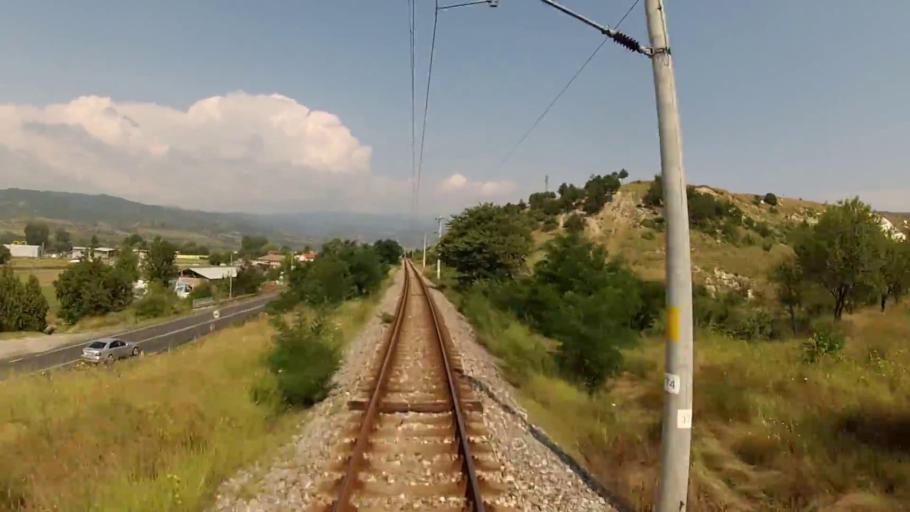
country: BG
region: Blagoevgrad
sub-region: Obshtina Strumyani
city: Strumyani
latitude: 41.6252
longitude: 23.2151
